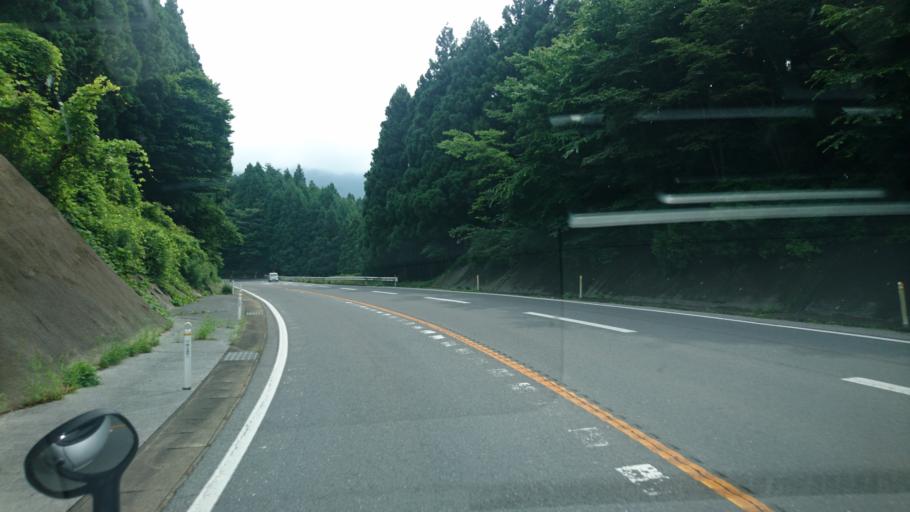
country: JP
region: Iwate
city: Ofunato
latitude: 39.1150
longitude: 141.8051
